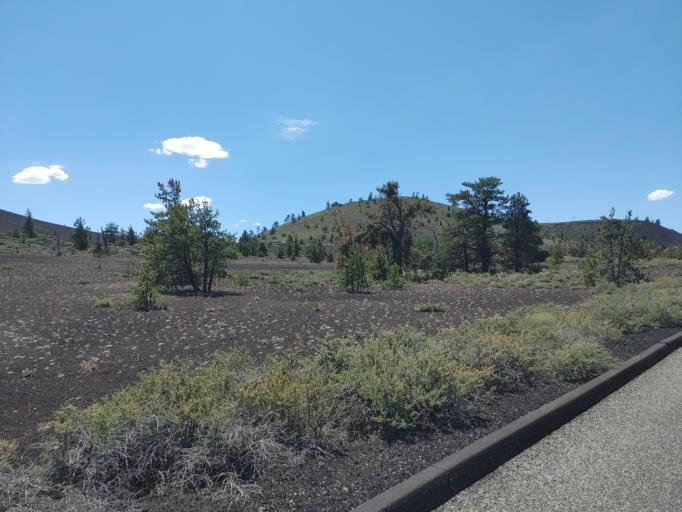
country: US
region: Idaho
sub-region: Butte County
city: Arco
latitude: 43.4470
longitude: -113.5530
